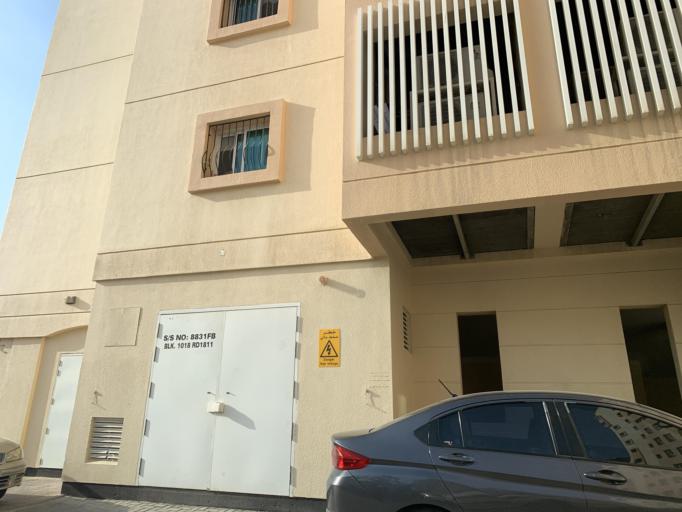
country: BH
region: Central Governorate
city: Madinat Hamad
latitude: 26.1212
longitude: 50.4873
